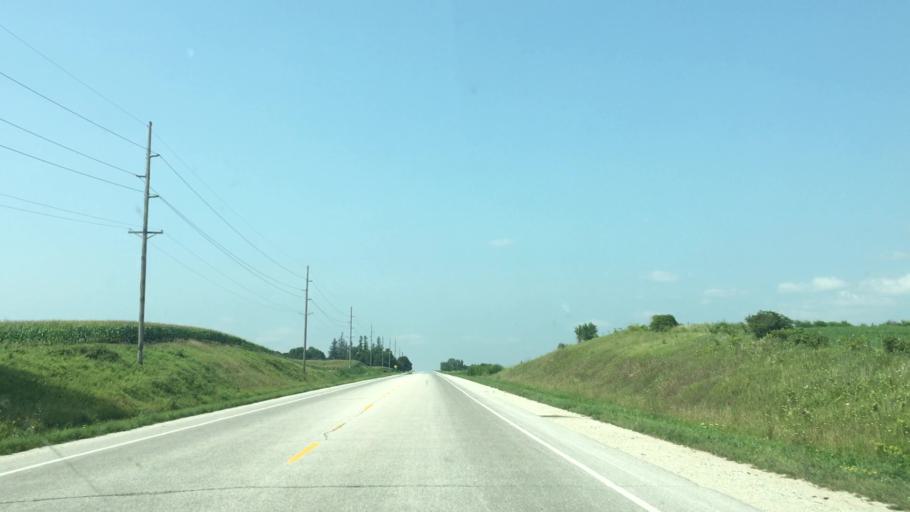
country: US
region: Minnesota
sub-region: Fillmore County
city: Harmony
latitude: 43.5443
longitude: -91.9296
